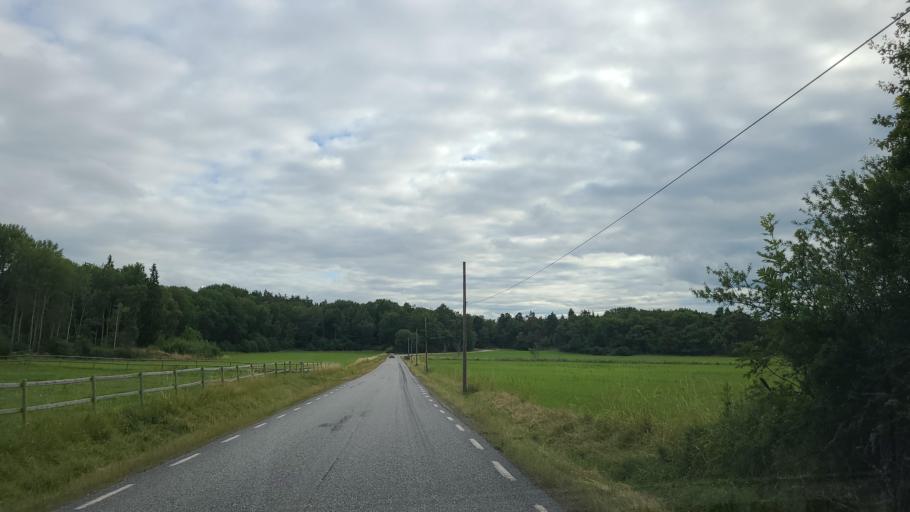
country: SE
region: Stockholm
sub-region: Upplands-Bro Kommun
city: Bro
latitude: 59.4744
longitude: 17.5957
